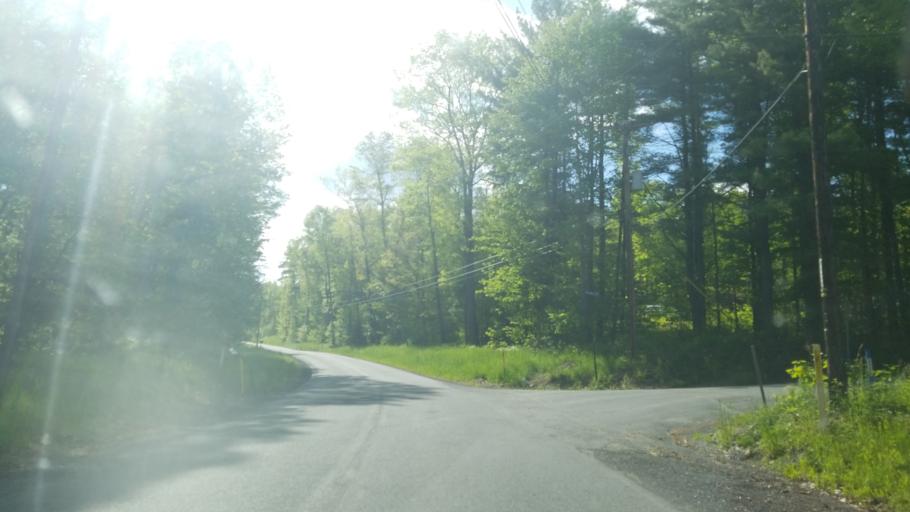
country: US
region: Pennsylvania
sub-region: Clearfield County
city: Troy
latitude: 40.9337
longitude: -78.3045
